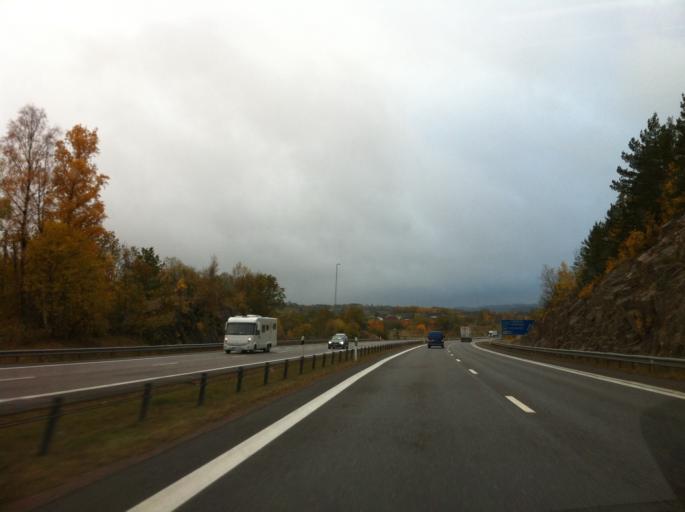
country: SE
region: Joenkoeping
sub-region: Jonkopings Kommun
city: Graenna
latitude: 58.0085
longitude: 14.4644
